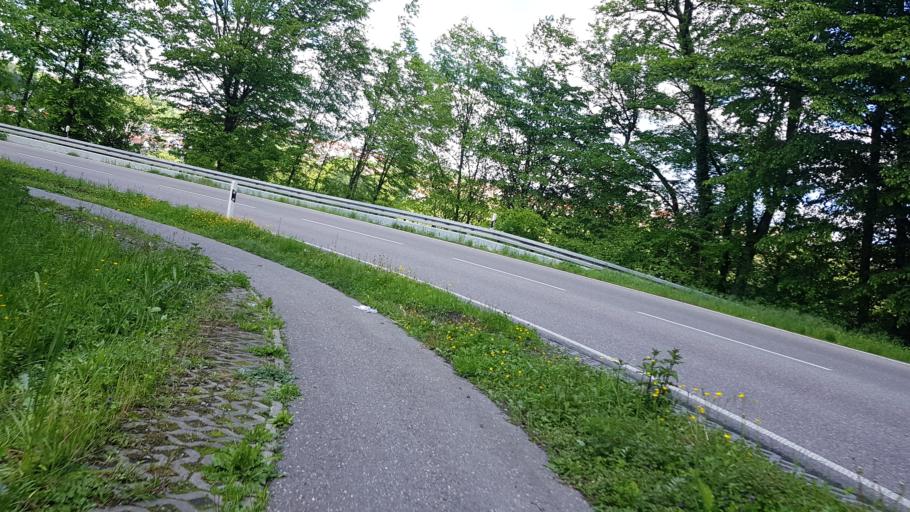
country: DE
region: Baden-Wuerttemberg
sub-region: Regierungsbezirk Stuttgart
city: Kirchberg an der Murr
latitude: 48.9354
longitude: 9.3331
